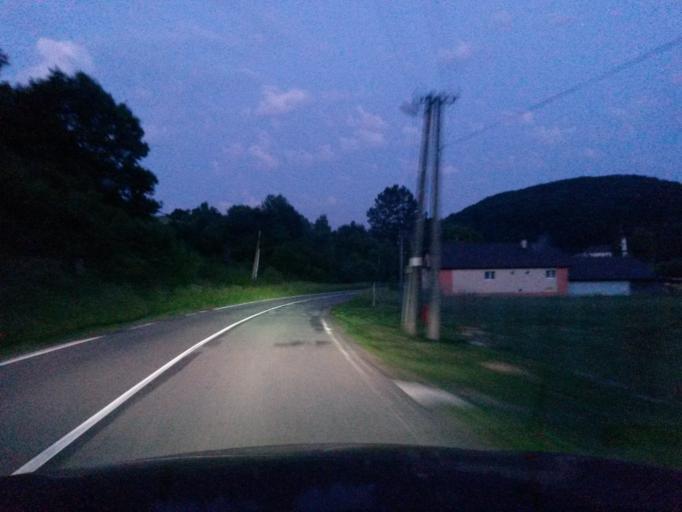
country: UA
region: Zakarpattia
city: Velykyi Bereznyi
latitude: 48.9248
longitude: 22.3164
